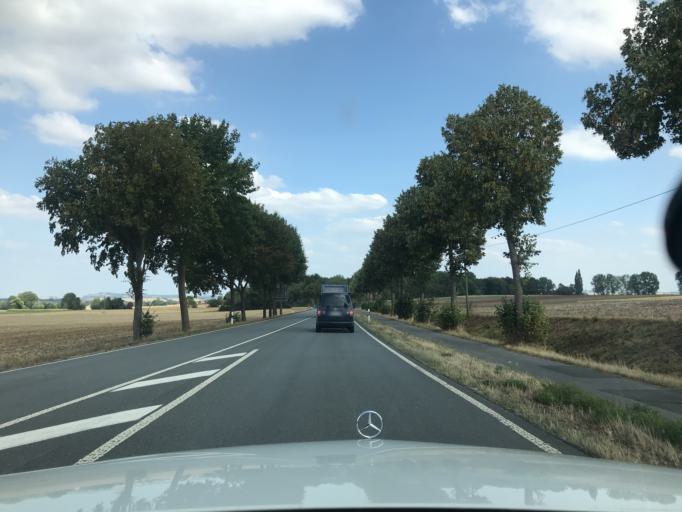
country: DE
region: North Rhine-Westphalia
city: Warburg
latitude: 51.5361
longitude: 9.1613
